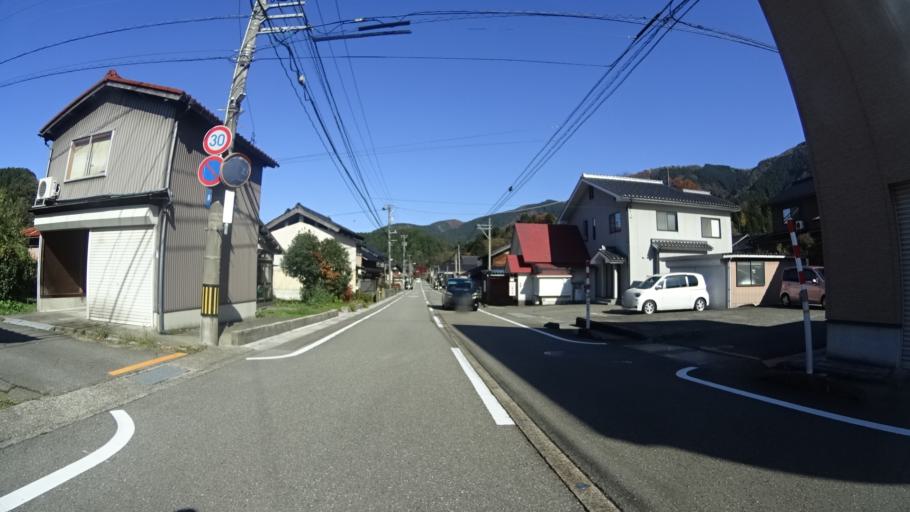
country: JP
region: Ishikawa
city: Tsurugi-asahimachi
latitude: 36.4310
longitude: 136.6339
